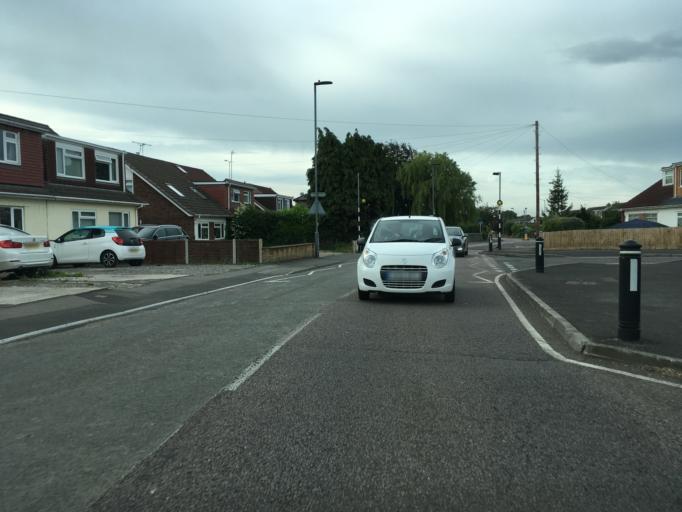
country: GB
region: England
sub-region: South Gloucestershire
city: Almondsbury
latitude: 51.5352
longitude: -2.5629
